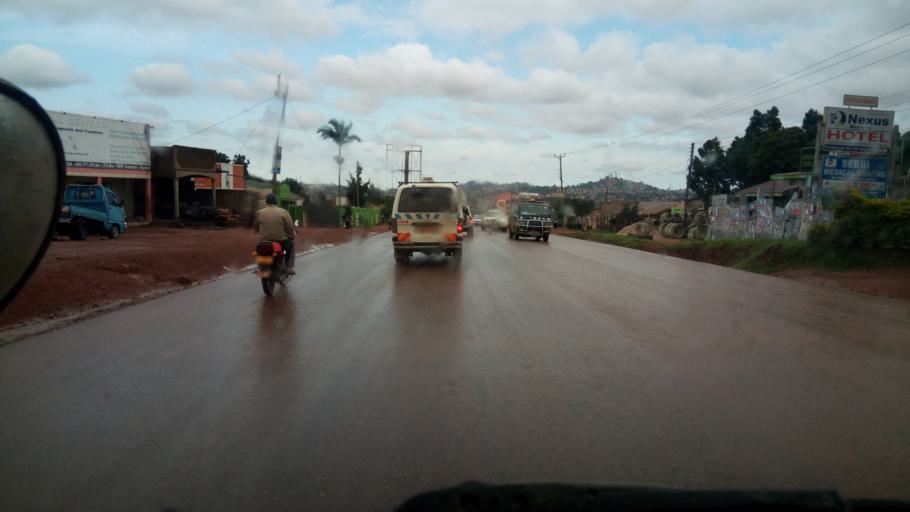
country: UG
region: Central Region
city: Kampala Central Division
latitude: 0.3568
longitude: 32.5338
